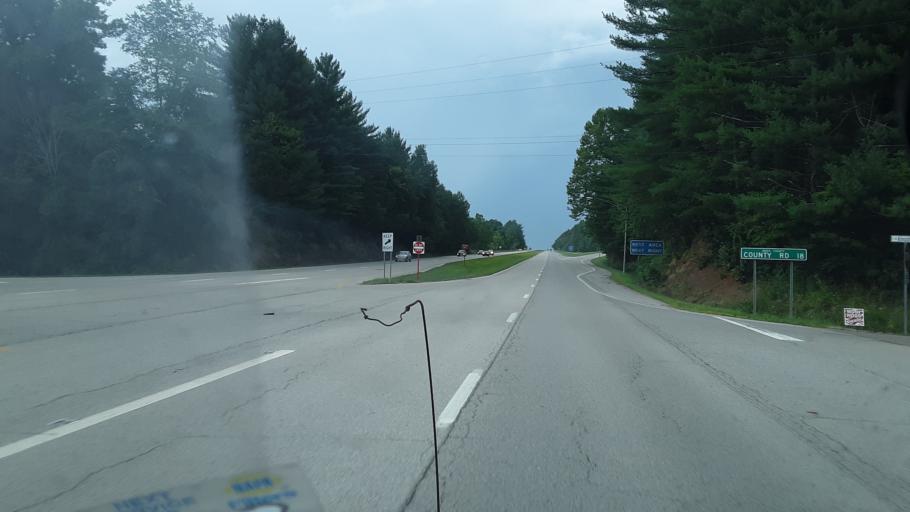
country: US
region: Ohio
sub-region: Meigs County
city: Pomeroy
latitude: 39.1138
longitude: -82.0154
